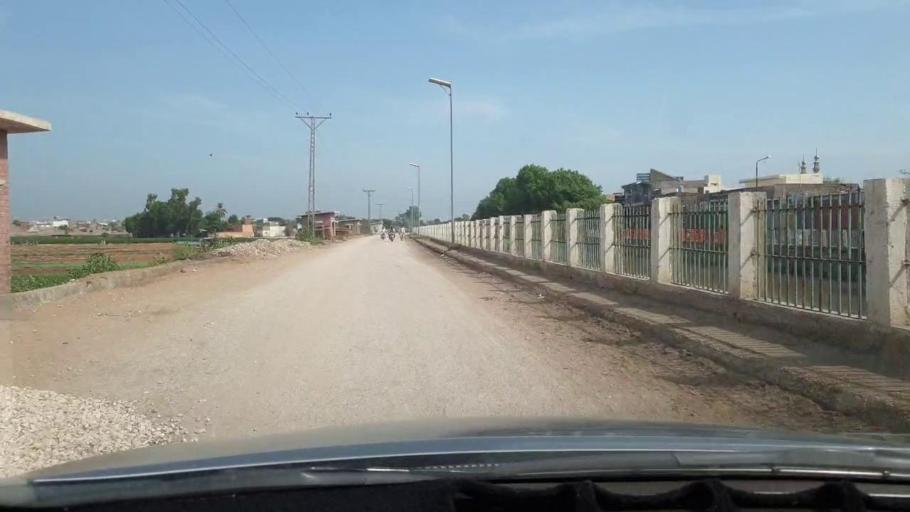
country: PK
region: Sindh
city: Khairpur
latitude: 27.5263
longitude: 68.7543
